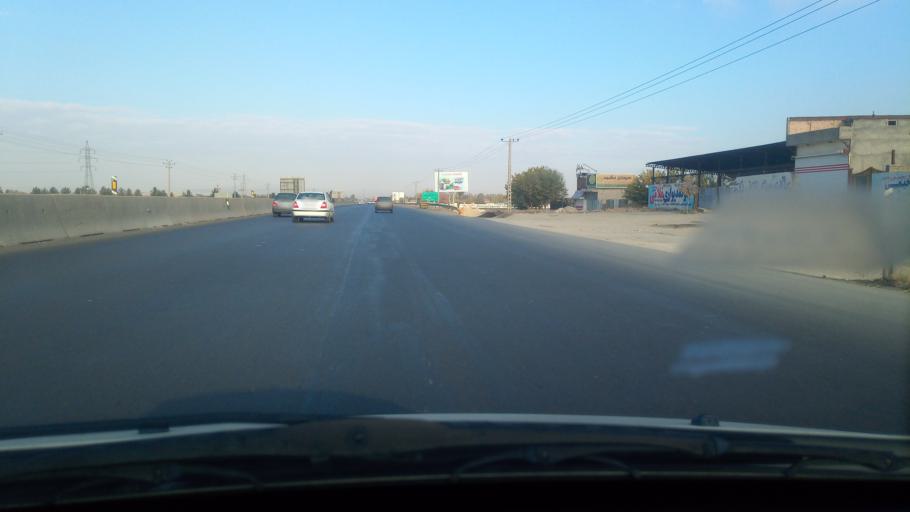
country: IR
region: Razavi Khorasan
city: Chenaran
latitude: 36.5420
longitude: 59.2755
